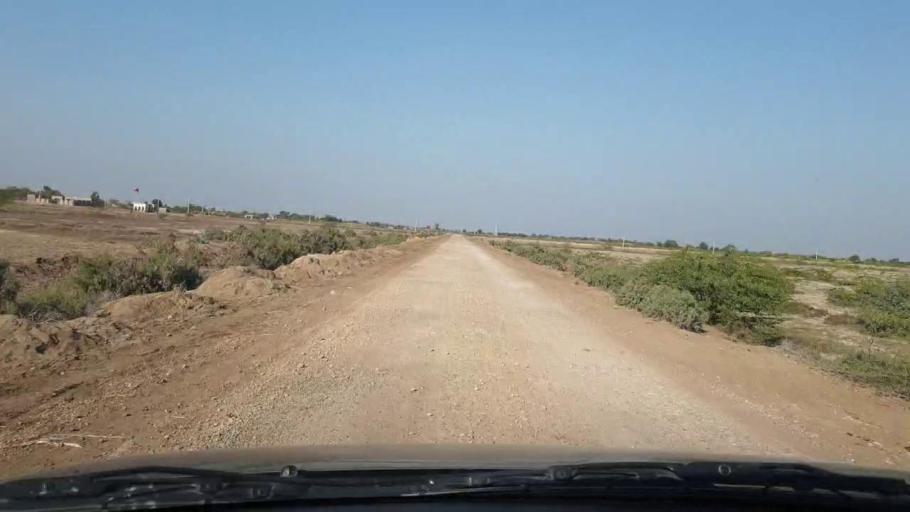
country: PK
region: Sindh
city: Digri
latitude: 25.1357
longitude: 69.2788
